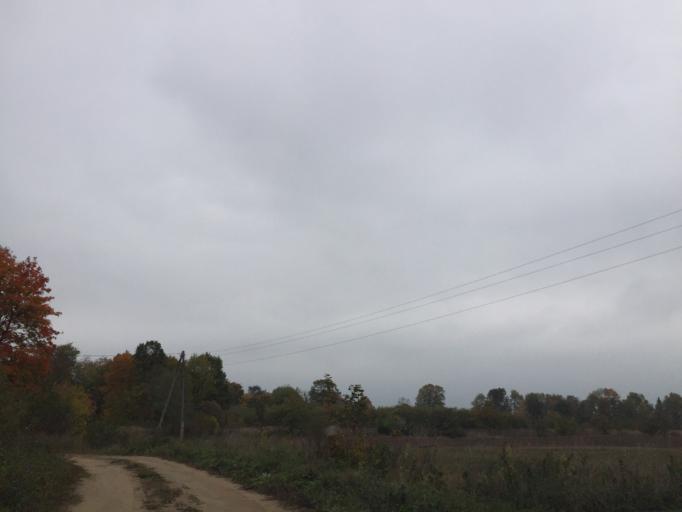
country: LV
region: Dobeles Rajons
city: Dobele
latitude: 56.6783
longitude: 23.4480
